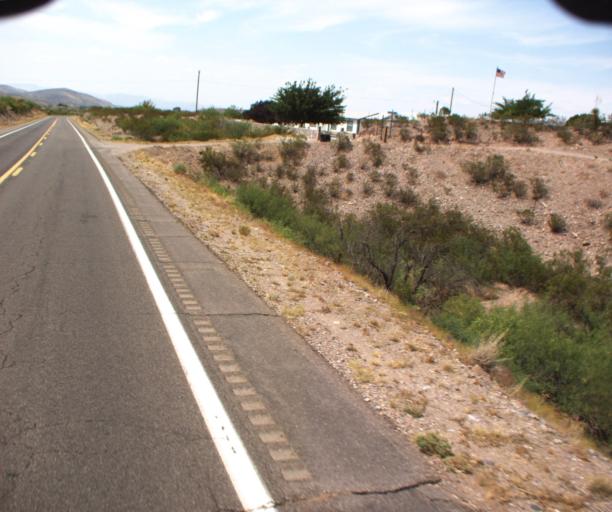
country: US
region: Arizona
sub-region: Greenlee County
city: Clifton
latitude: 32.8124
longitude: -109.1690
